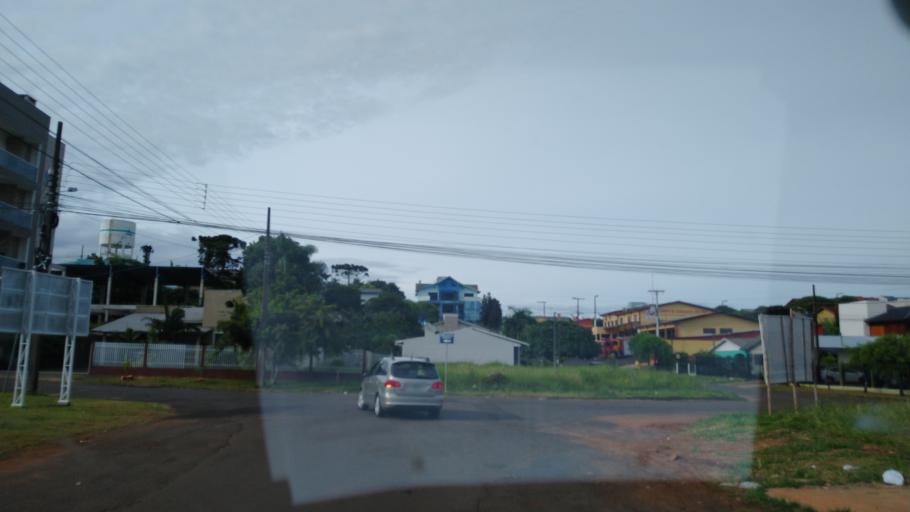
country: AR
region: Misiones
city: Bernardo de Irigoyen
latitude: -26.2602
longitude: -53.6330
